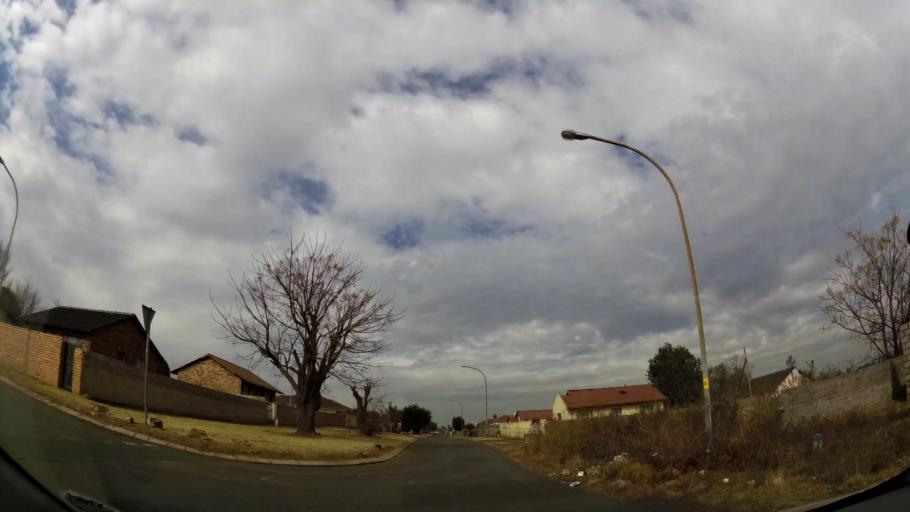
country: ZA
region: Gauteng
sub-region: Ekurhuleni Metropolitan Municipality
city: Germiston
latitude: -26.3206
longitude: 28.1757
